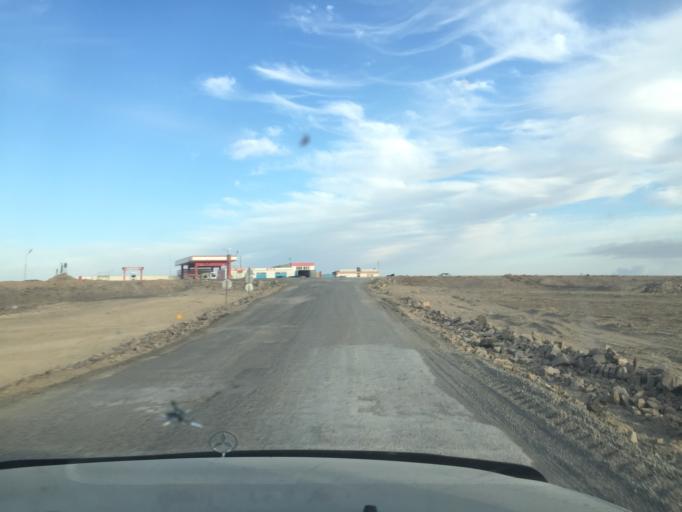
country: KZ
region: Almaty Oblysy
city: Ulken
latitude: 45.1542
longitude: 73.9484
